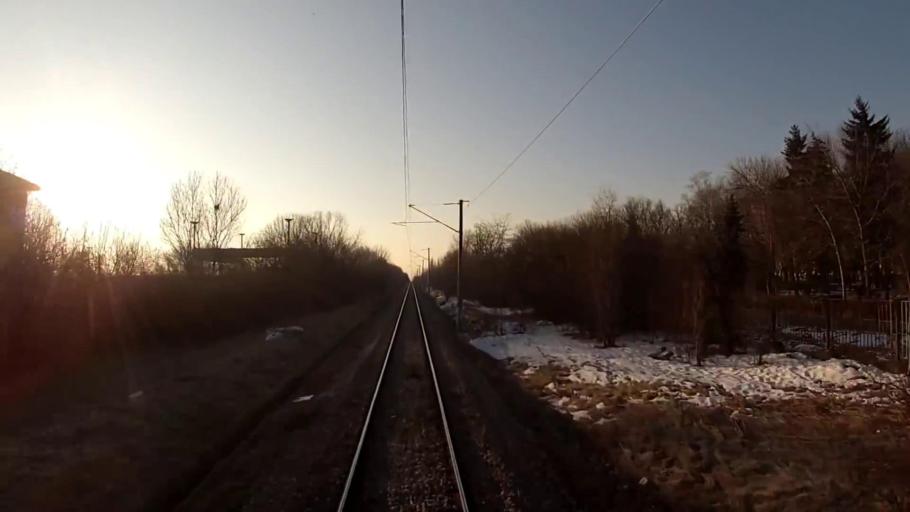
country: BG
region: Sofiya
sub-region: Obshtina Kostinbrod
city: Kostinbrod
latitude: 42.7891
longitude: 23.2117
